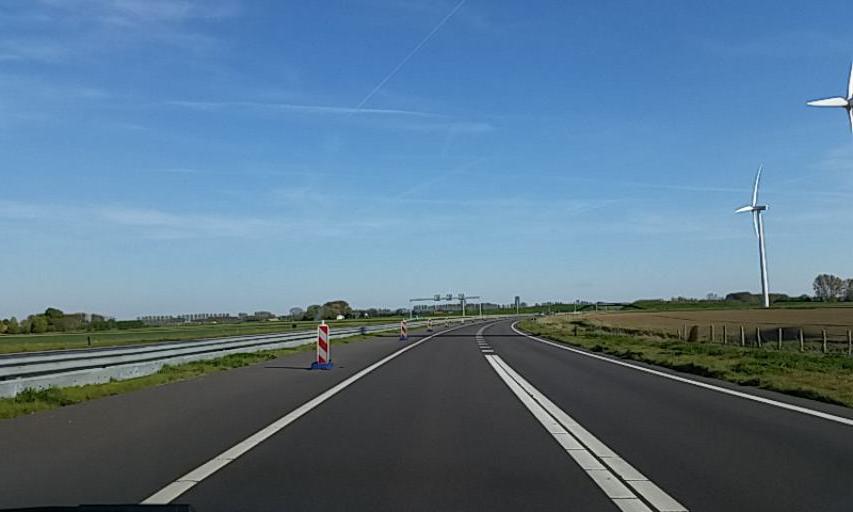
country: NL
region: Zeeland
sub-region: Gemeente Terneuzen
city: Sluiskil
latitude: 51.2919
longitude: 3.8666
